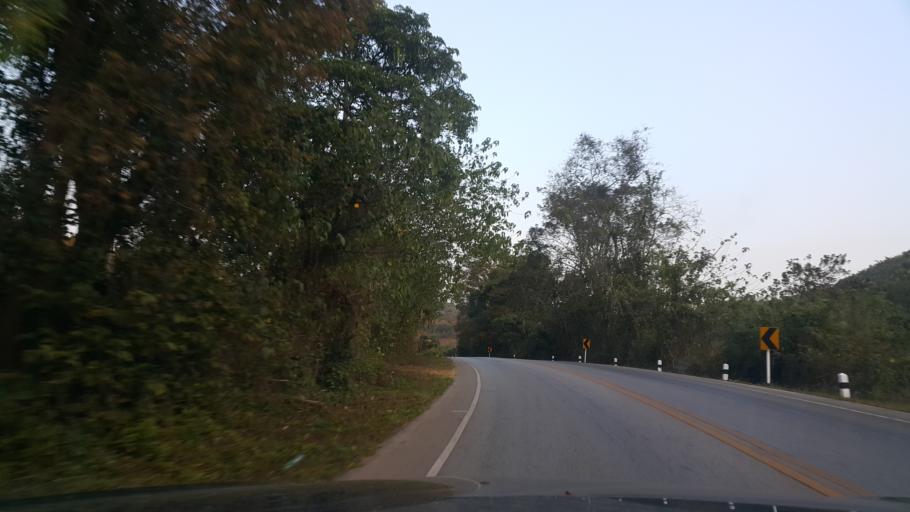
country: TH
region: Loei
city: Loei
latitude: 17.4670
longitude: 101.5891
